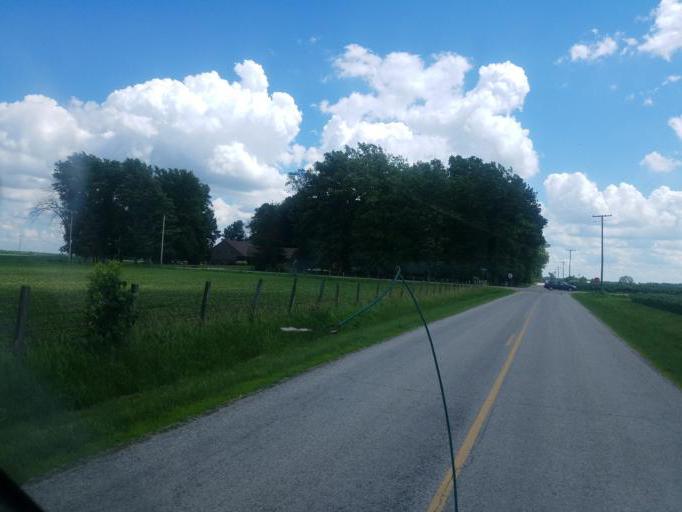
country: US
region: Ohio
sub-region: Crawford County
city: Galion
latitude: 40.8299
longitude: -82.8376
